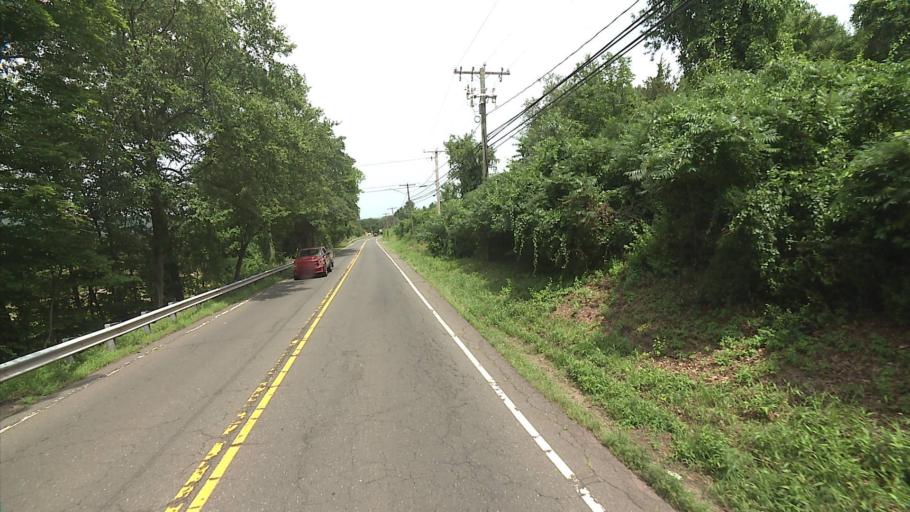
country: US
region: Connecticut
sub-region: Hartford County
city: Kensington
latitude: 41.5954
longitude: -72.7986
